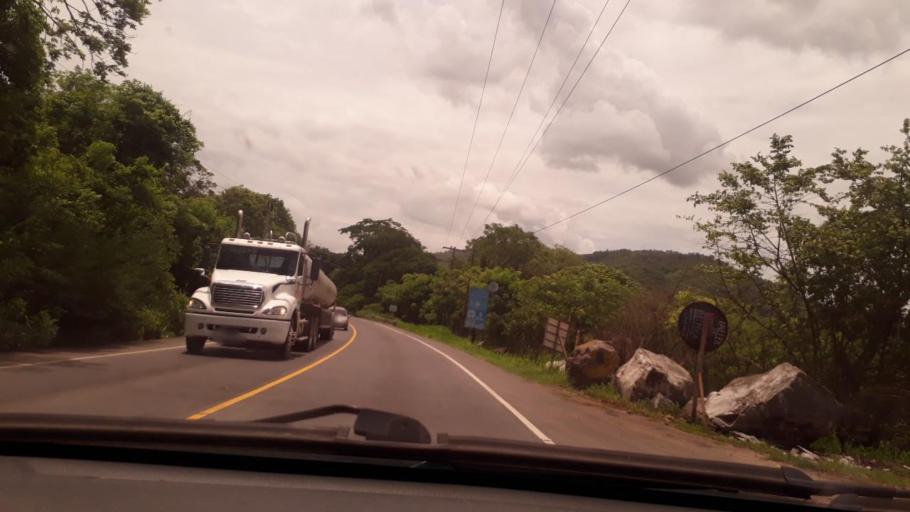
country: GT
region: Zacapa
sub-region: Municipio de Zacapa
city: Gualan
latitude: 15.1625
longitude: -89.3121
